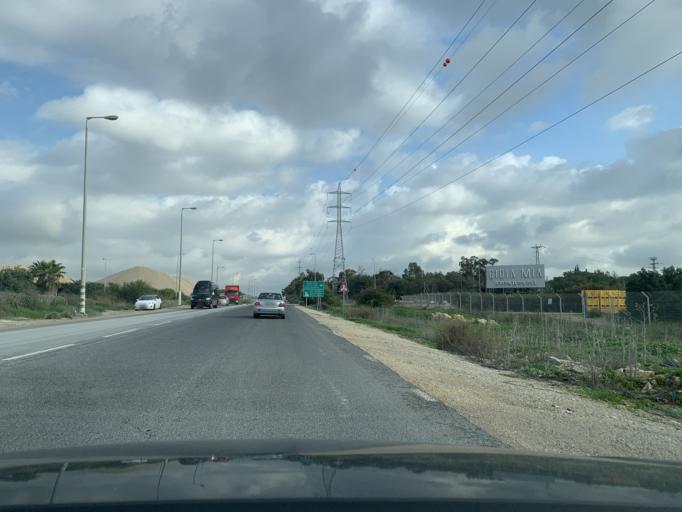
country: IL
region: Central District
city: Rosh Ha'Ayin
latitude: 32.0671
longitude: 34.9458
